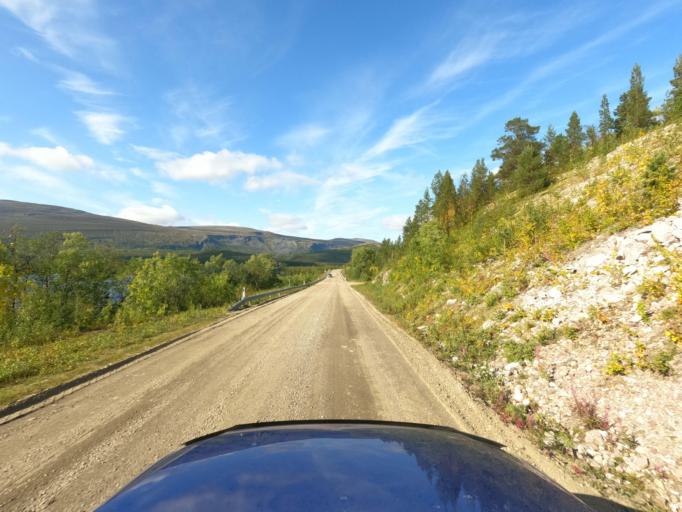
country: NO
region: Finnmark Fylke
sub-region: Porsanger
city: Lakselv
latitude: 69.8909
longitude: 25.0007
